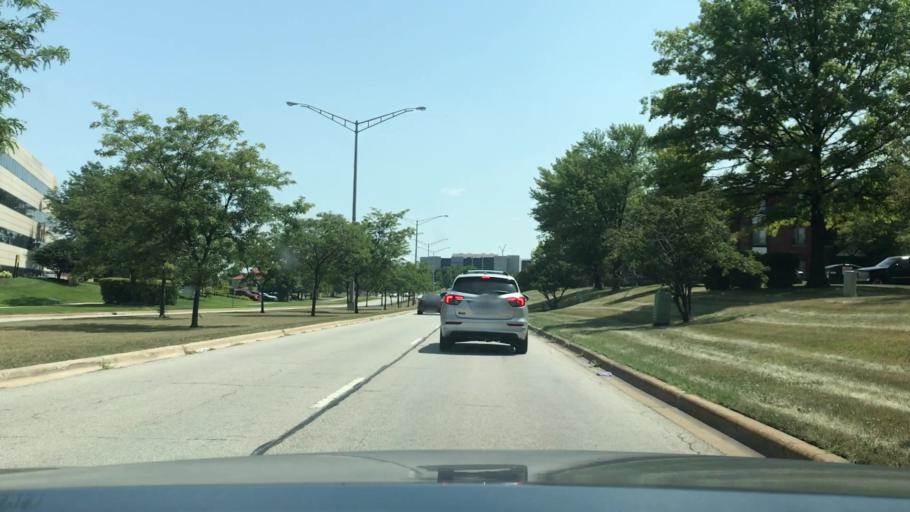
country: US
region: Illinois
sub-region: DuPage County
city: Warrenville
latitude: 41.7570
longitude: -88.2198
